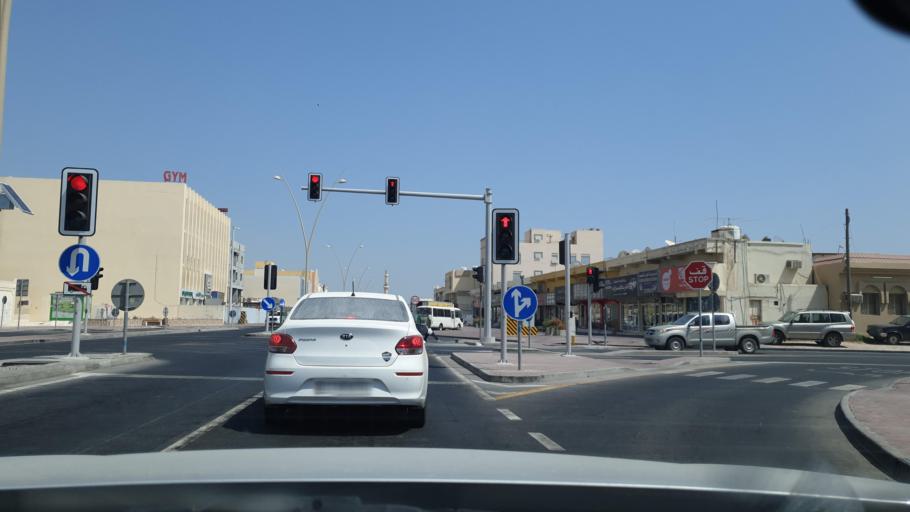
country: QA
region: Al Khawr
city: Al Khawr
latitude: 25.6826
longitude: 51.5022
